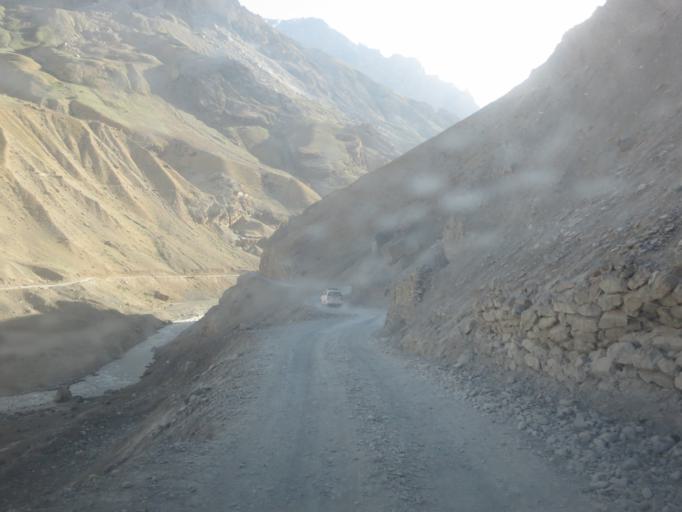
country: IN
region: Himachal Pradesh
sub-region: Kulu
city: Manali
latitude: 32.3289
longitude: 77.9234
